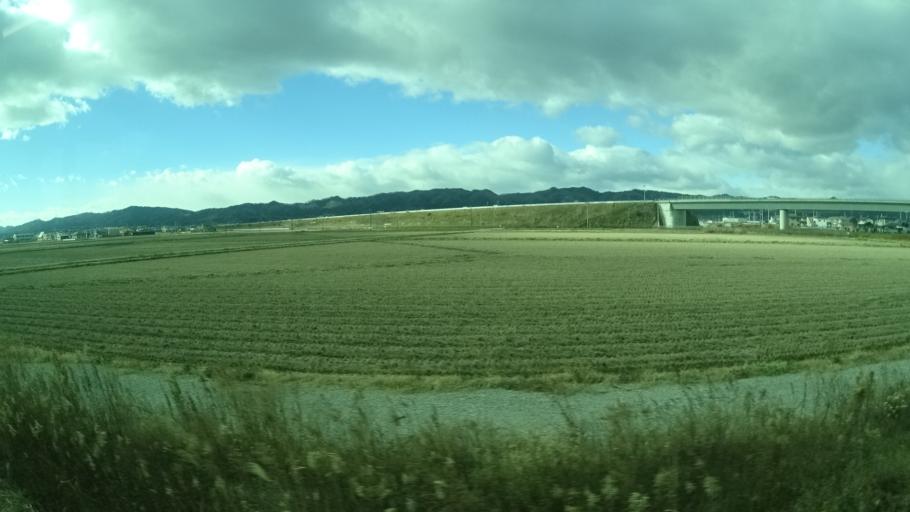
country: JP
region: Miyagi
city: Watari
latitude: 38.0128
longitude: 140.8862
